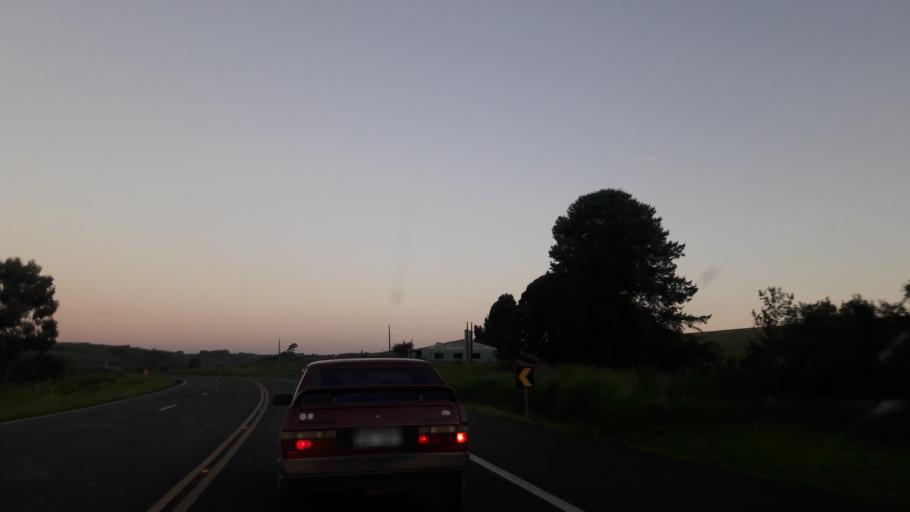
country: BR
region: Parana
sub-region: Palmeira
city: Palmeira
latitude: -25.4341
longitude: -50.0570
